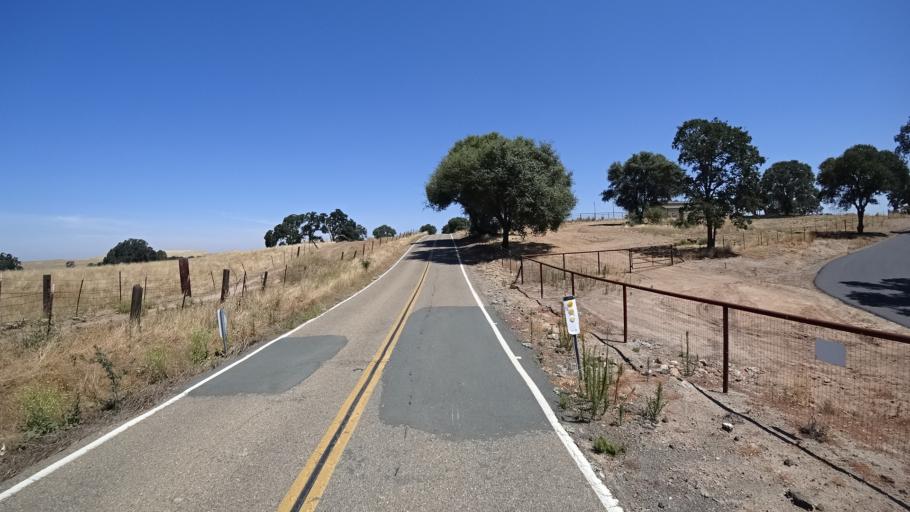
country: US
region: California
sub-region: Calaveras County
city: Rancho Calaveras
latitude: 38.1242
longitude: -120.9449
